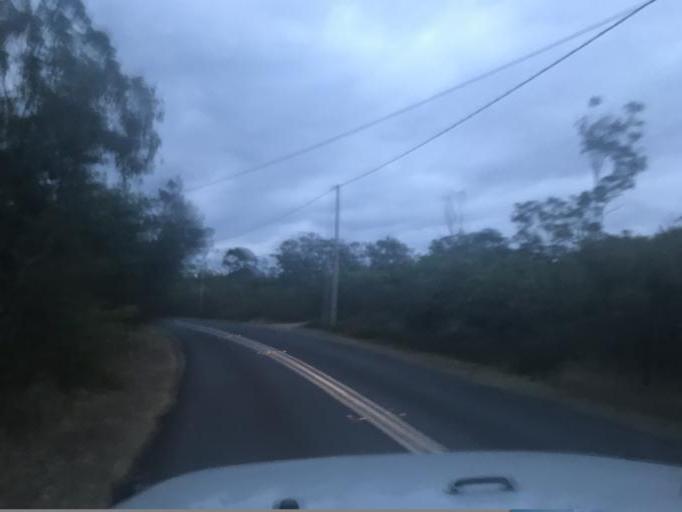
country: AU
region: New South Wales
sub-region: Hawkesbury
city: Pitt Town
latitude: -33.4732
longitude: 150.8629
